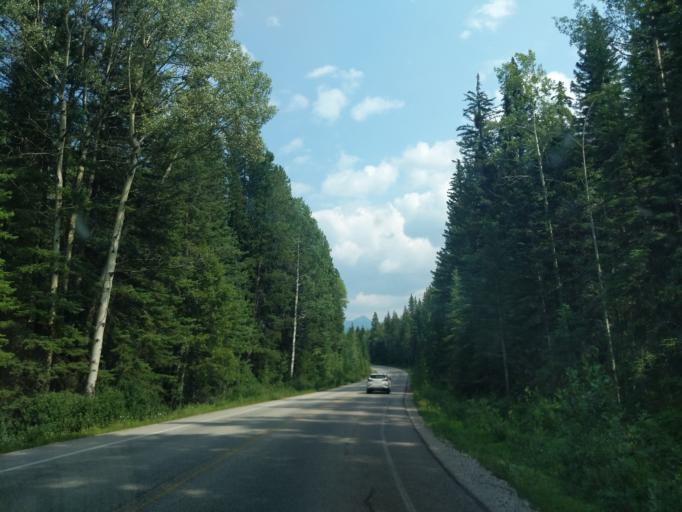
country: CA
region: Alberta
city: Banff
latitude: 51.1731
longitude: -115.7100
